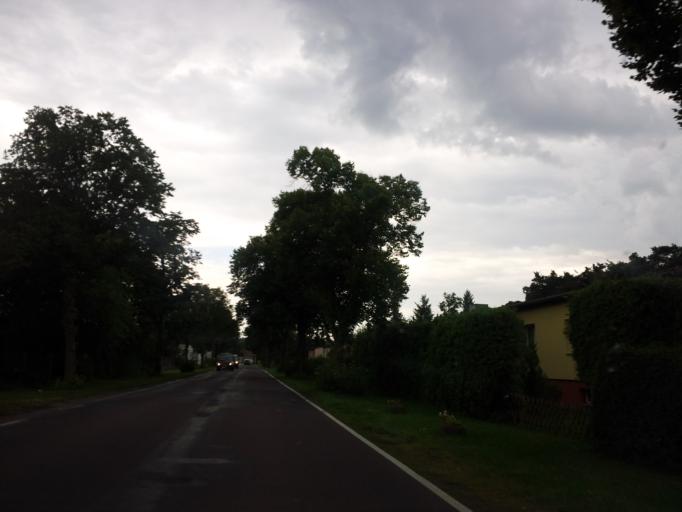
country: DE
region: Brandenburg
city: Wollin
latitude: 52.2855
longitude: 12.4661
